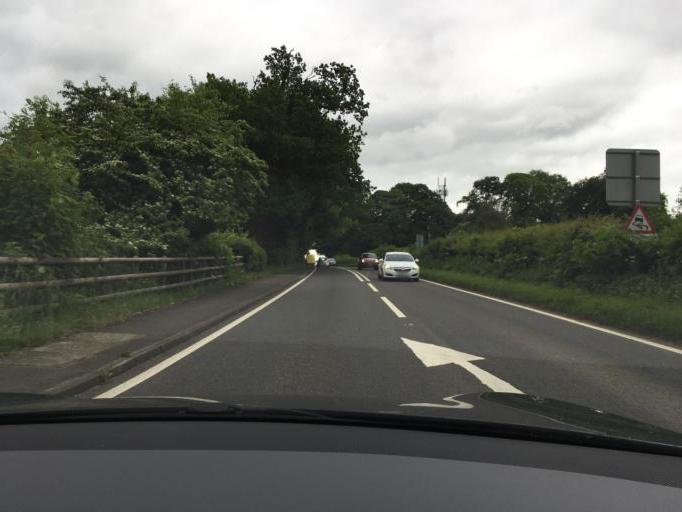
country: GB
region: England
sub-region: Derbyshire
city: Yeldersley
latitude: 52.9855
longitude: -1.6764
